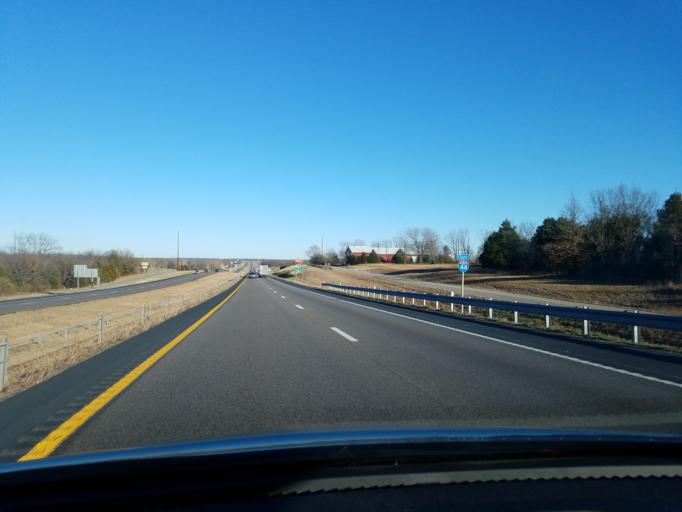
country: US
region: Missouri
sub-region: Phelps County
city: Rolla
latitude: 37.9805
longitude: -91.7118
